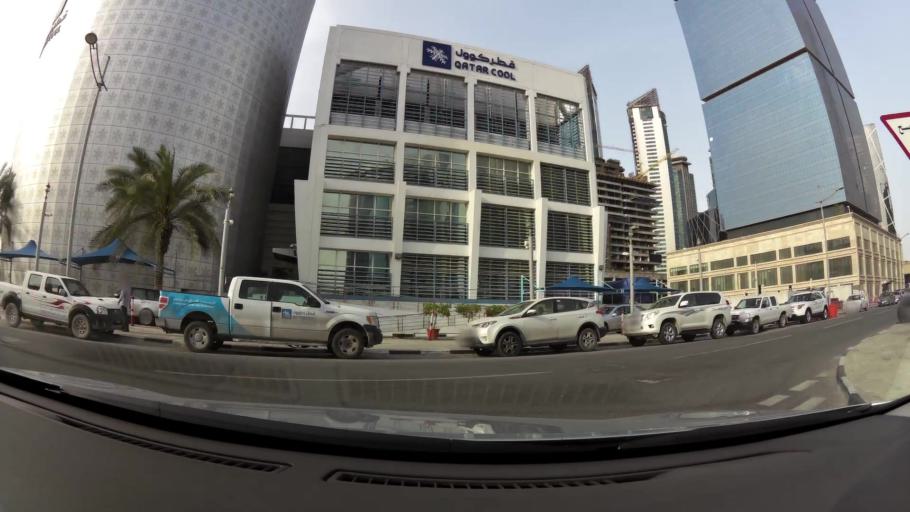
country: QA
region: Baladiyat ad Dawhah
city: Doha
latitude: 25.3219
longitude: 51.5242
